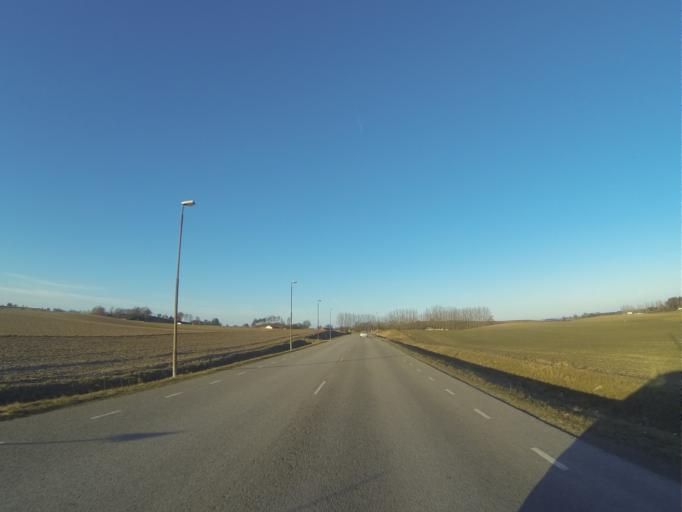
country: SE
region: Skane
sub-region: Malmo
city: Oxie
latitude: 55.5582
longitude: 13.1055
